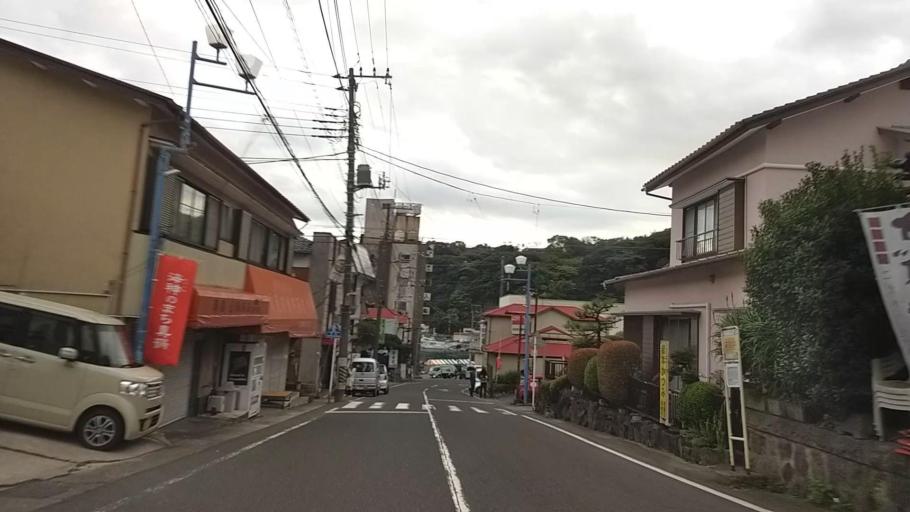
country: JP
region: Kanagawa
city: Yugawara
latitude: 35.1548
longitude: 139.1418
